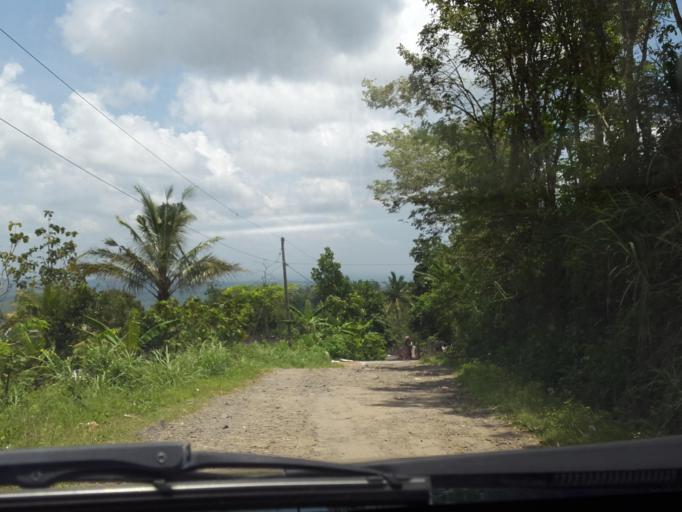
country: ID
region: Daerah Istimewa Yogyakarta
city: Wonosari
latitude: -7.9070
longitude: 110.7499
